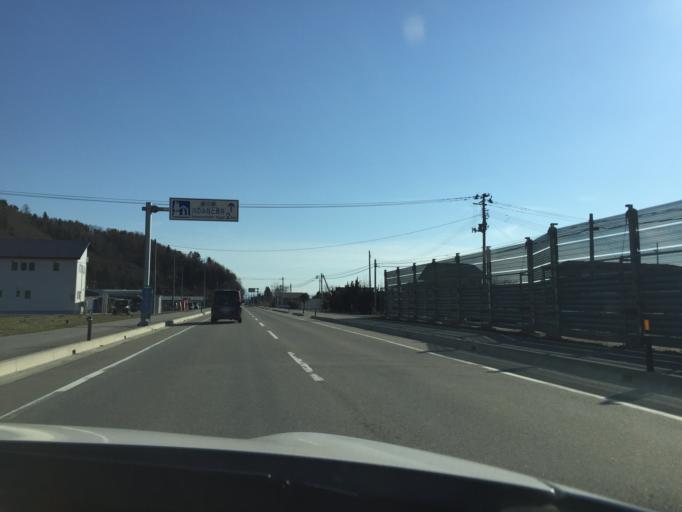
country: JP
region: Yamagata
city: Nagai
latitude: 38.1242
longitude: 140.0551
